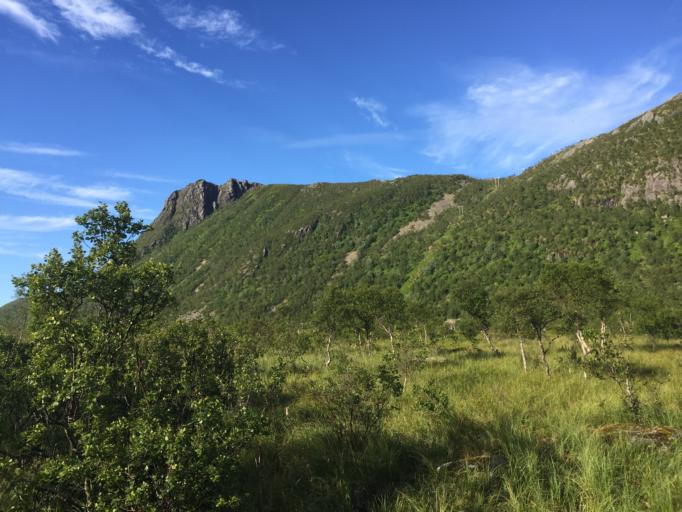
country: NO
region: Nordland
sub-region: Vagan
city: Kabelvag
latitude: 68.2976
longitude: 14.4324
